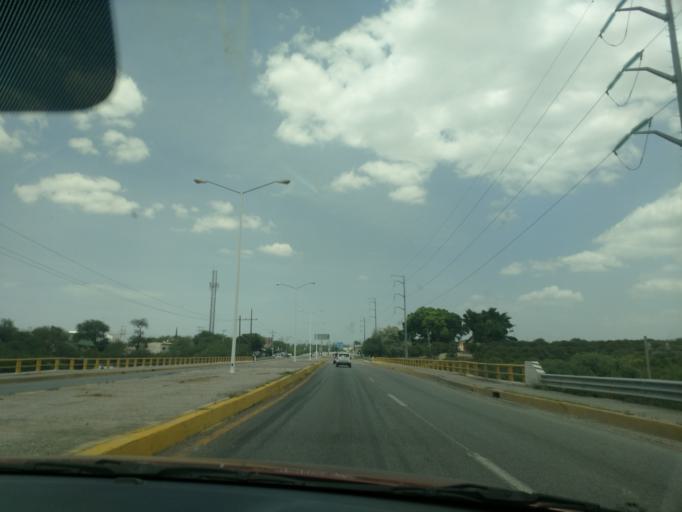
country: MX
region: San Luis Potosi
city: Rio Verde
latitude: 21.9217
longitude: -99.9662
